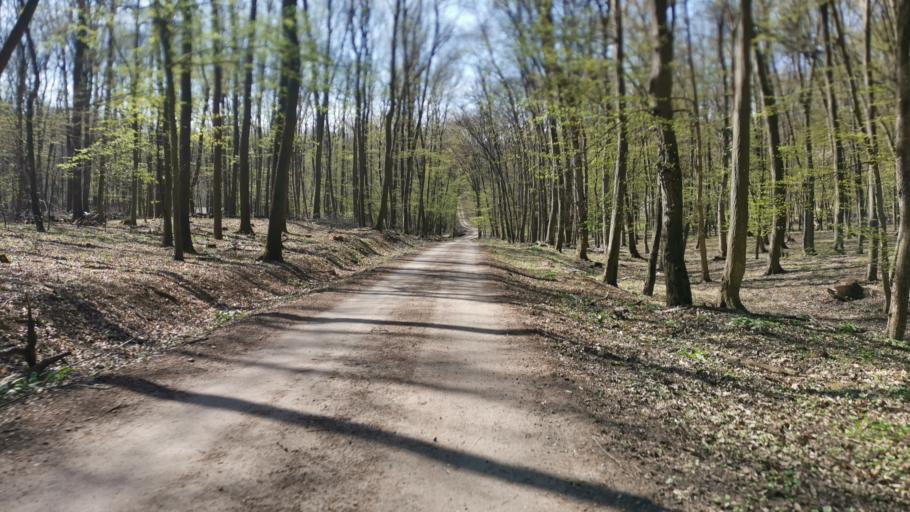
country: SK
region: Trnavsky
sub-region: Okres Skalica
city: Holic
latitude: 48.7369
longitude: 17.2396
